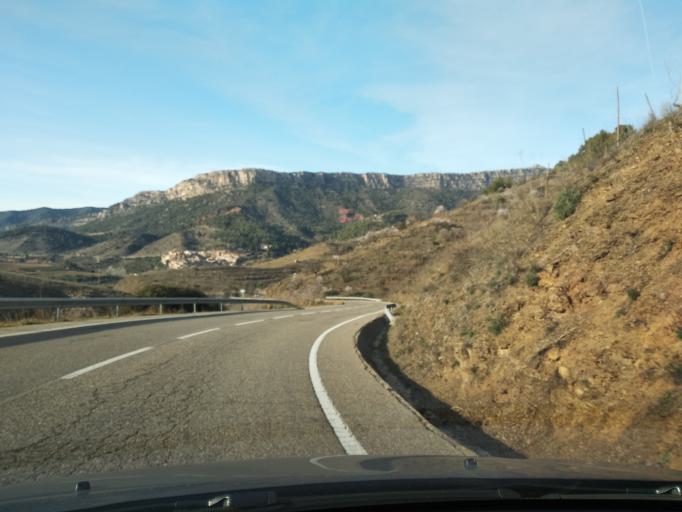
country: ES
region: Catalonia
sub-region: Provincia de Tarragona
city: Margalef
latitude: 41.2130
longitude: 0.7696
